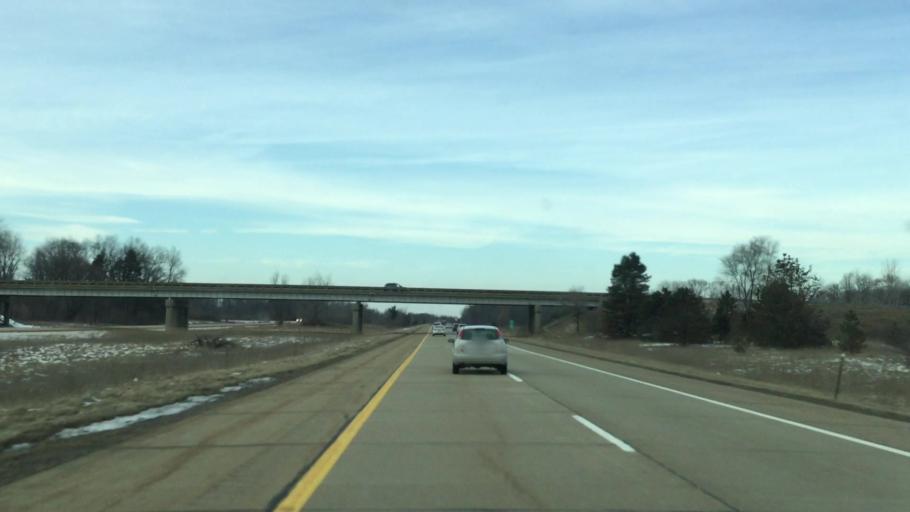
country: US
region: Michigan
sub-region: Calhoun County
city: Marshall
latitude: 42.3487
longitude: -84.9811
